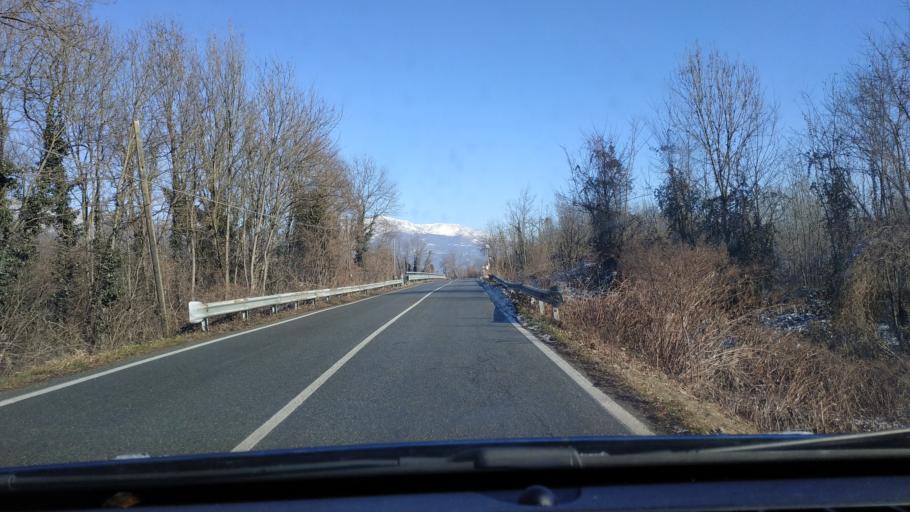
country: IT
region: Piedmont
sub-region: Provincia di Torino
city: Parella
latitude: 45.4190
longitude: 7.7972
